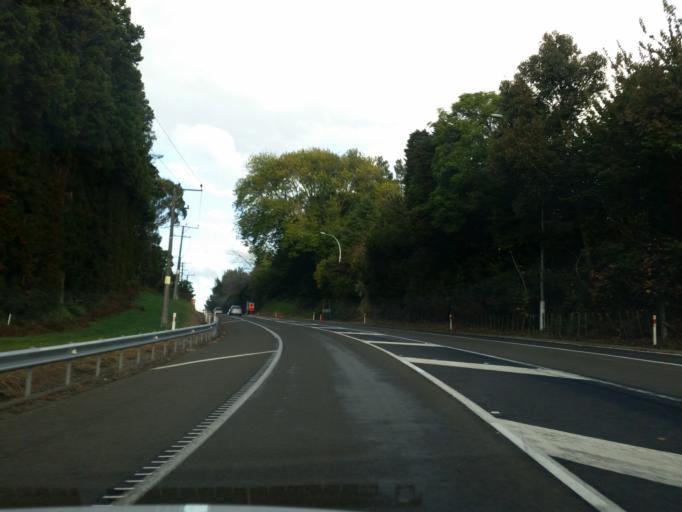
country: NZ
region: Bay of Plenty
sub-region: Western Bay of Plenty District
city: Katikati
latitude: -37.6544
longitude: 175.9966
